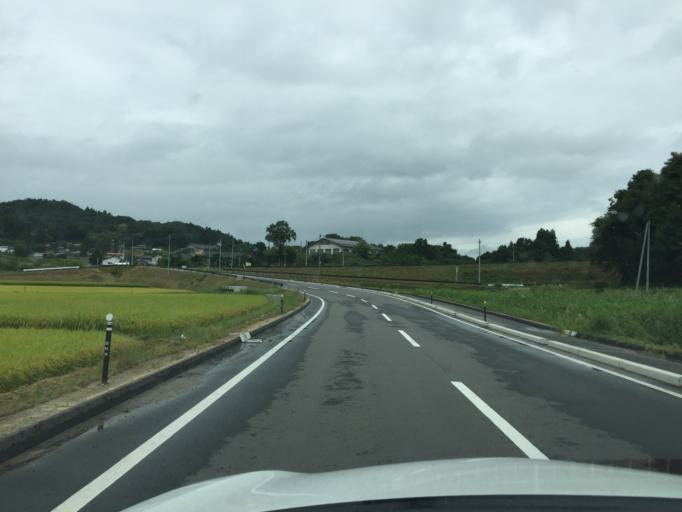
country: JP
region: Fukushima
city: Funehikimachi-funehiki
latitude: 37.4482
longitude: 140.5585
